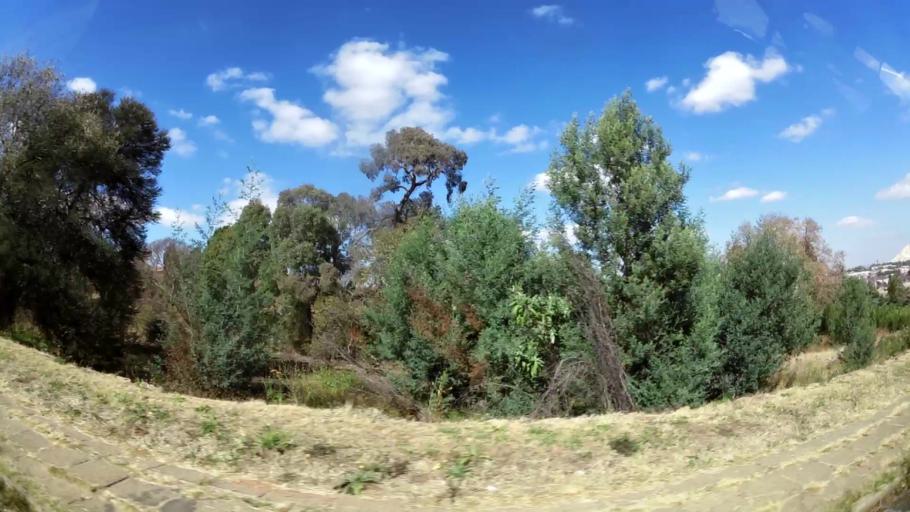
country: ZA
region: Gauteng
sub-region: West Rand District Municipality
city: Krugersdorp
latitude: -26.0964
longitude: 27.7840
